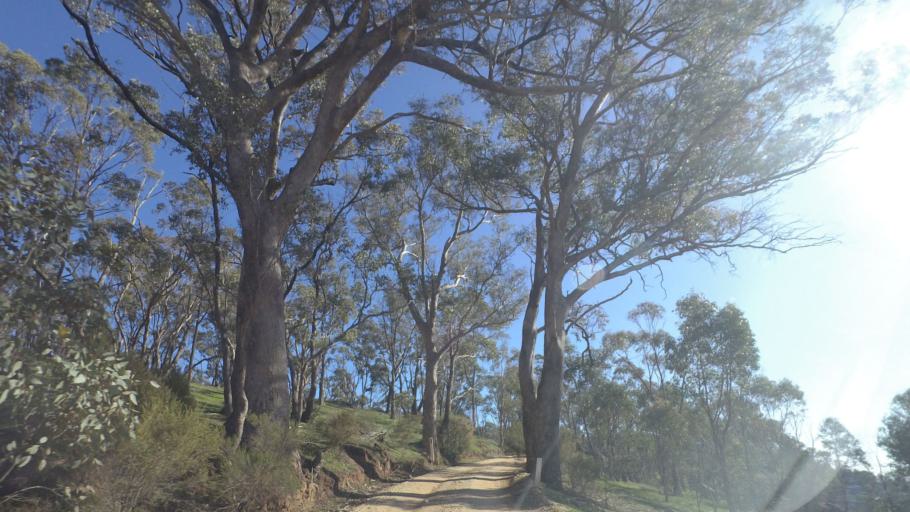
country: AU
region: Victoria
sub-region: Mount Alexander
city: Castlemaine
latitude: -37.0323
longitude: 144.2729
